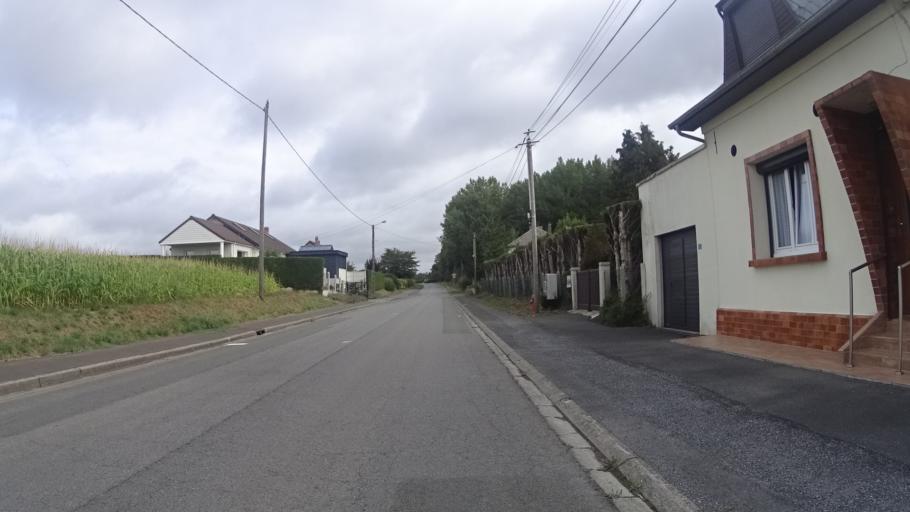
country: FR
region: Picardie
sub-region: Departement de l'Aisne
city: Boue
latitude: 50.0014
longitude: 3.6904
